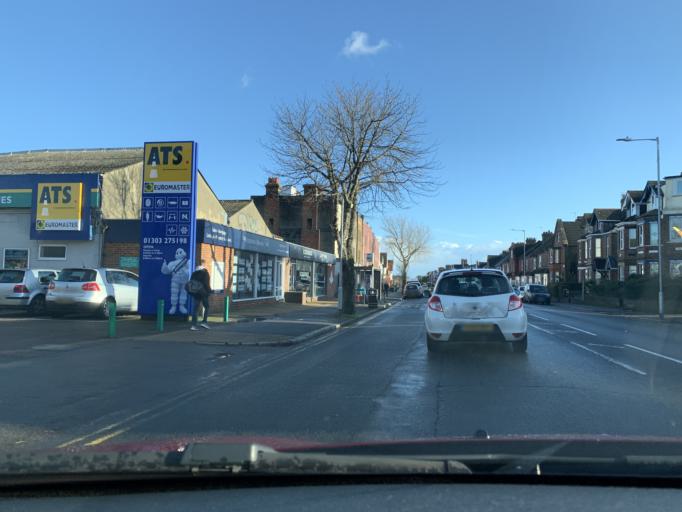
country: GB
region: England
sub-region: Kent
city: Hawkinge
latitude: 51.0868
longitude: 1.1502
